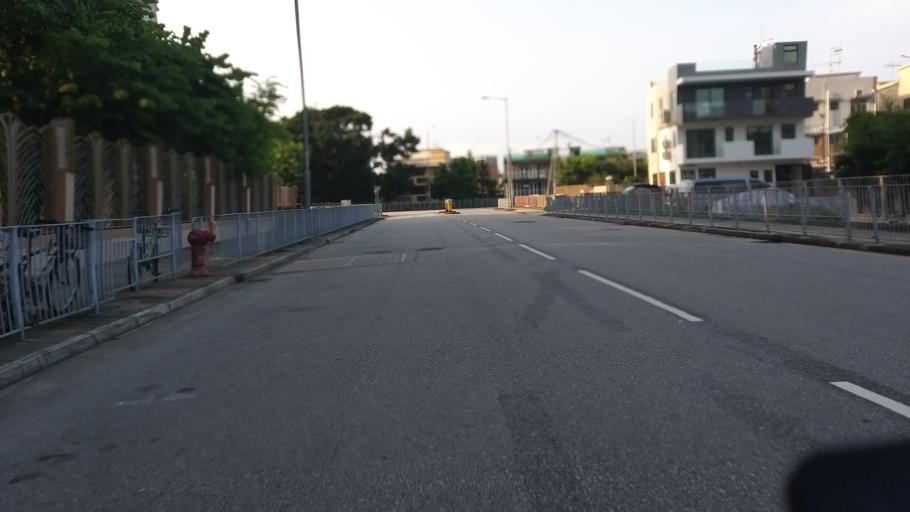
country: HK
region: Yuen Long
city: Yuen Long Kau Hui
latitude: 22.4508
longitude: 114.0336
